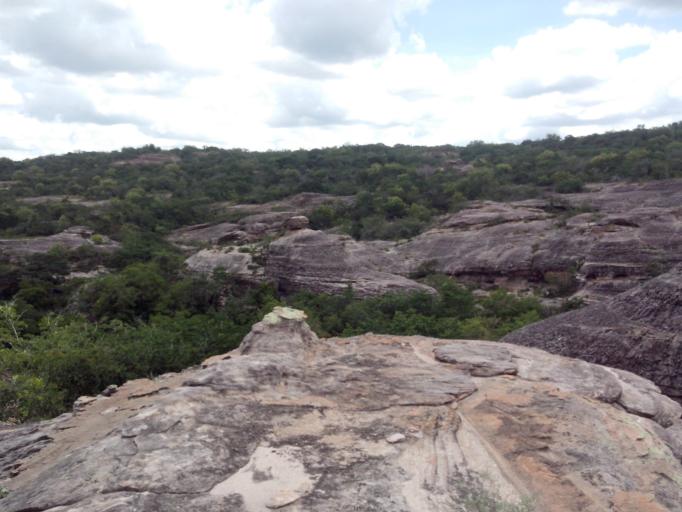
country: BR
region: Piaui
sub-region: Sao Raimundo Nonato
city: Sao Raimundo Nonato
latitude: -8.6493
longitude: -42.7022
